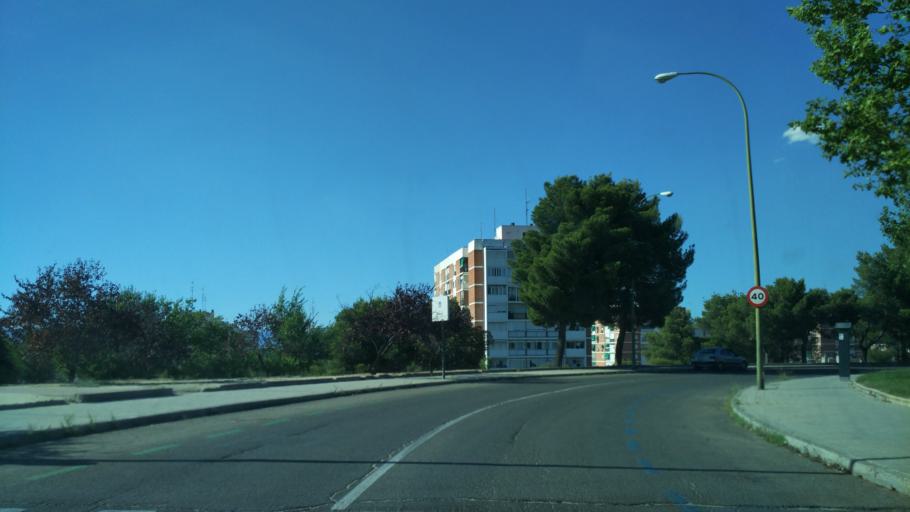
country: ES
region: Madrid
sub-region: Provincia de Madrid
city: Tetuan de las Victorias
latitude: 40.4746
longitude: -3.7096
